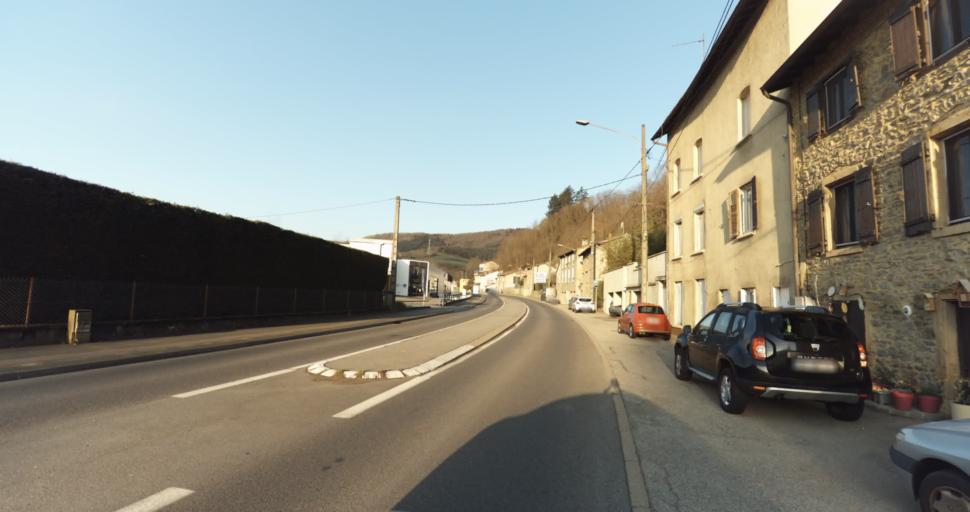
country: FR
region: Rhone-Alpes
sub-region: Departement du Rhone
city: Tarare
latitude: 45.8969
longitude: 4.4170
